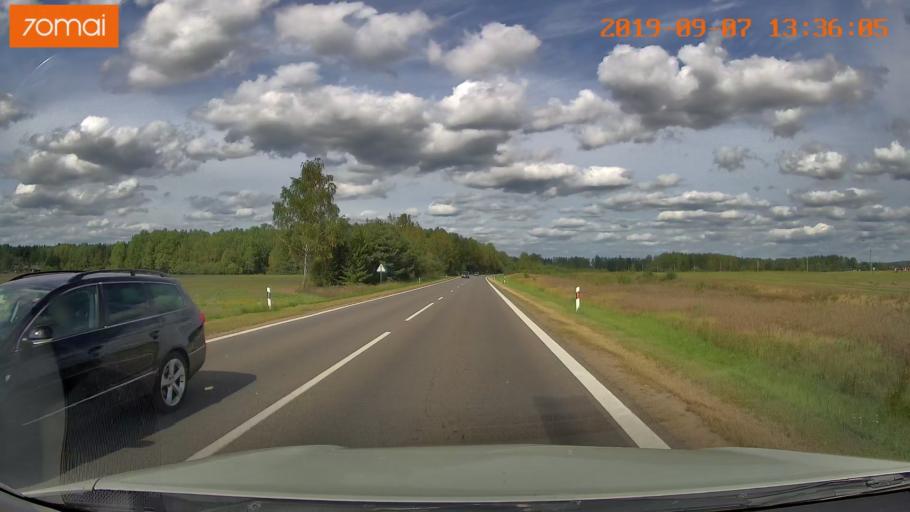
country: LT
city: Skaidiskes
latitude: 54.5193
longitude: 25.3140
